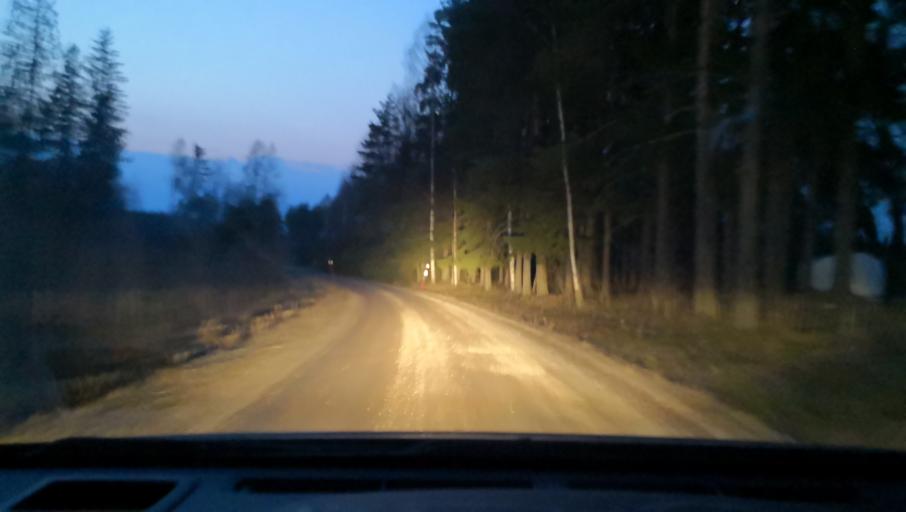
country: SE
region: OErebro
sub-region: Lindesbergs Kommun
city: Frovi
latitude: 59.5949
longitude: 15.4690
